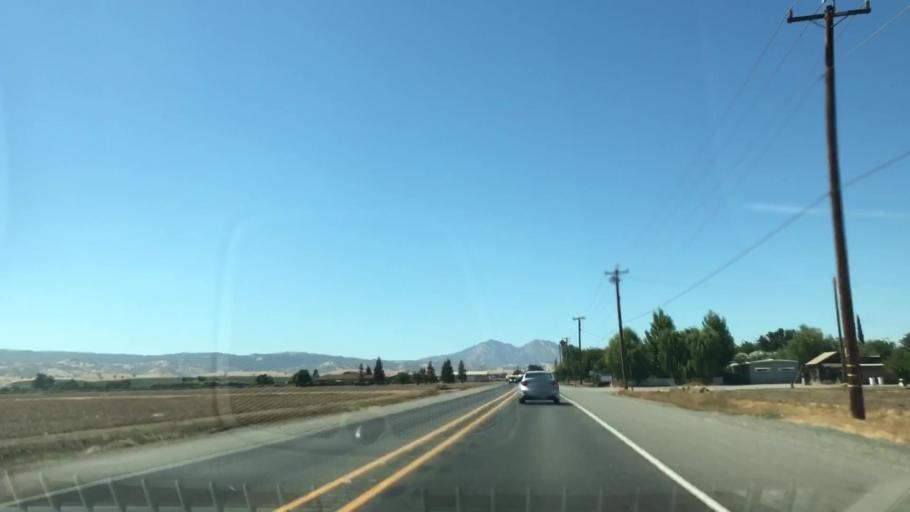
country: US
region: California
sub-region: Contra Costa County
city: Byron
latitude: 37.8966
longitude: -121.6540
